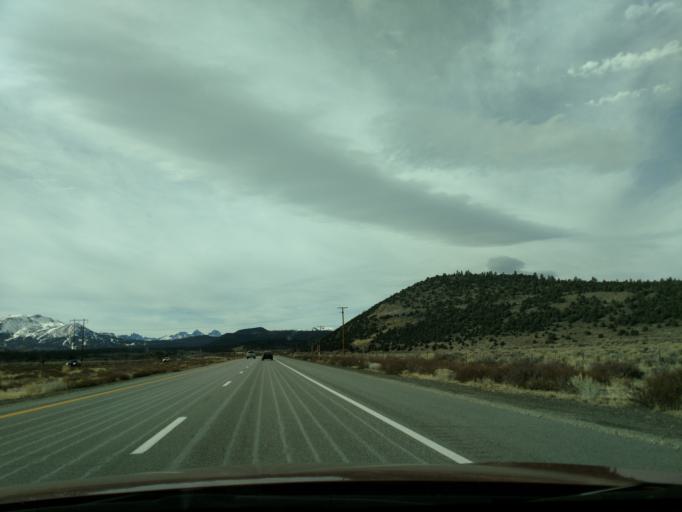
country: US
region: California
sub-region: Mono County
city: Mammoth Lakes
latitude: 37.6343
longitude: -118.8816
